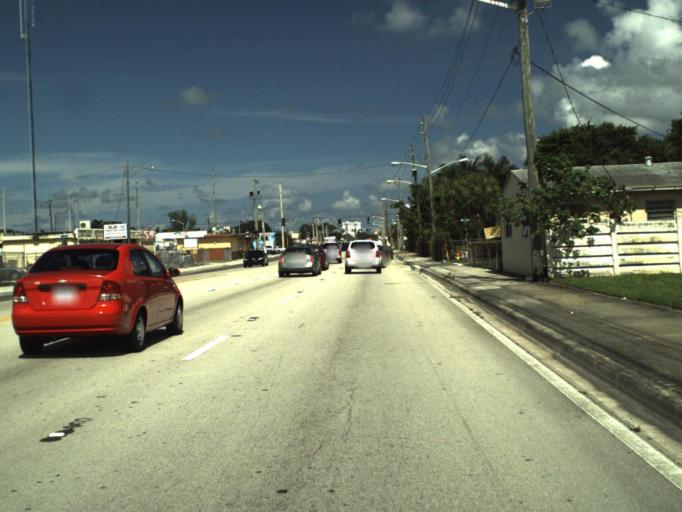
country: US
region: Florida
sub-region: Broward County
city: Hollywood
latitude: 25.9964
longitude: -80.1525
